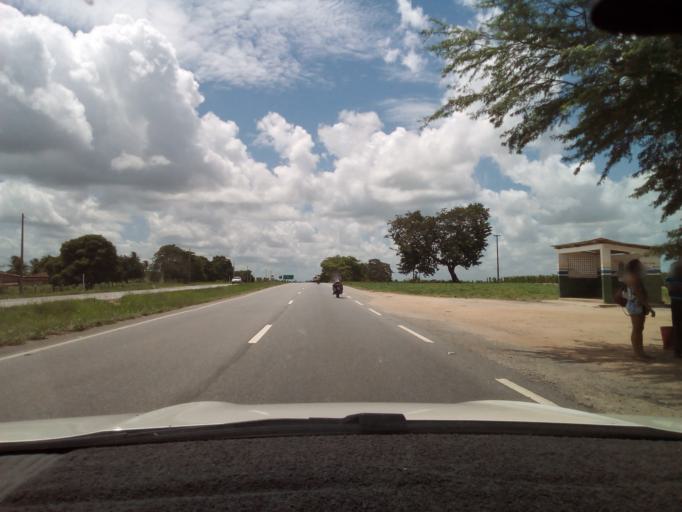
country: BR
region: Paraiba
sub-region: Pilar
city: Pilar
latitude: -7.1865
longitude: -35.2892
